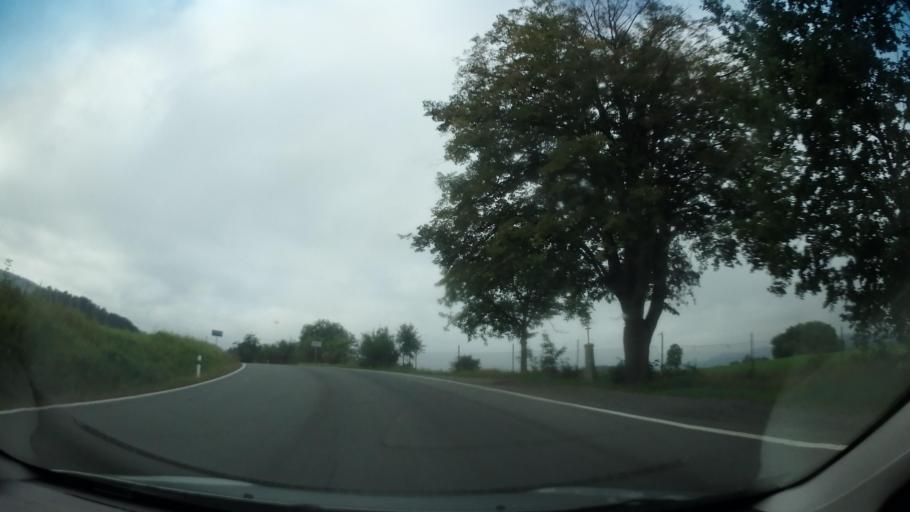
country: CZ
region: Central Bohemia
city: Kosova Hora
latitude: 49.7142
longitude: 14.4580
